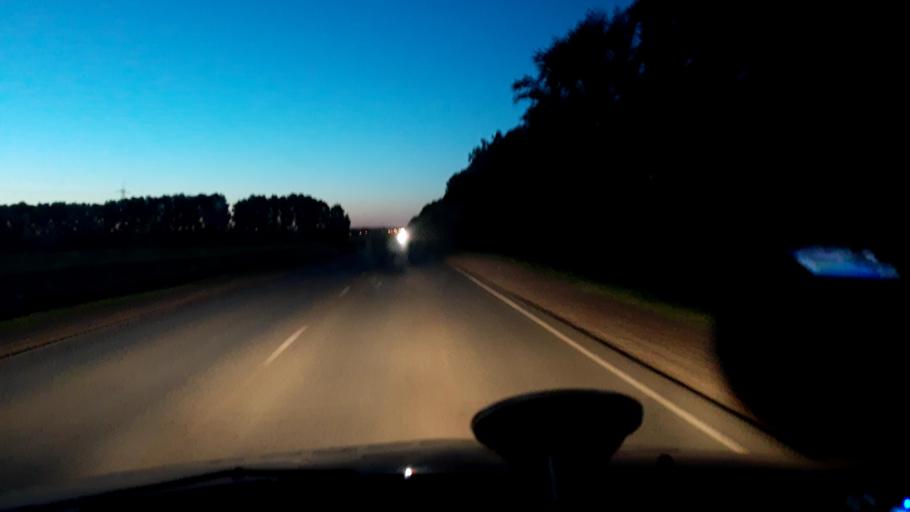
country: RU
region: Bashkortostan
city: Chishmy
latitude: 54.6489
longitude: 55.3849
